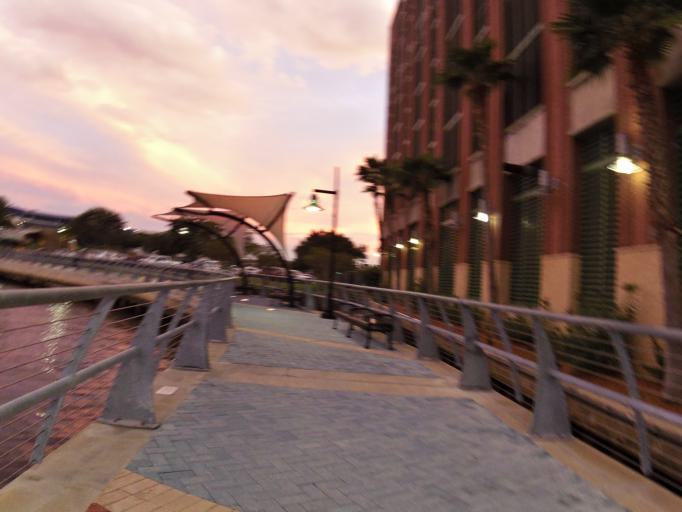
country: US
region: Florida
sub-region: Duval County
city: Jacksonville
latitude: 30.3193
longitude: -81.6544
